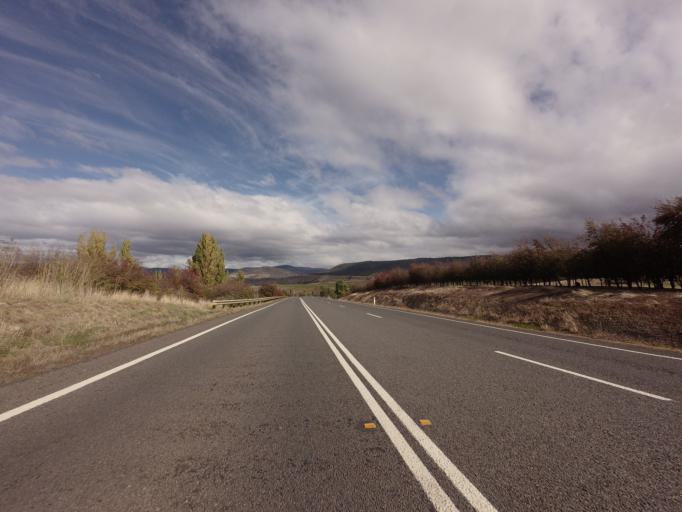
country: AU
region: Tasmania
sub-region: Derwent Valley
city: New Norfolk
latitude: -42.7184
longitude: 146.9482
